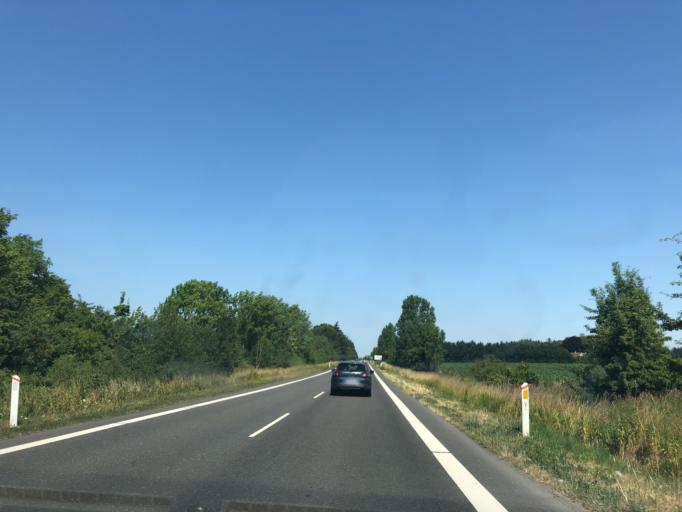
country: DK
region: Zealand
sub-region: Slagelse Kommune
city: Skaelskor
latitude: 55.2507
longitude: 11.3245
